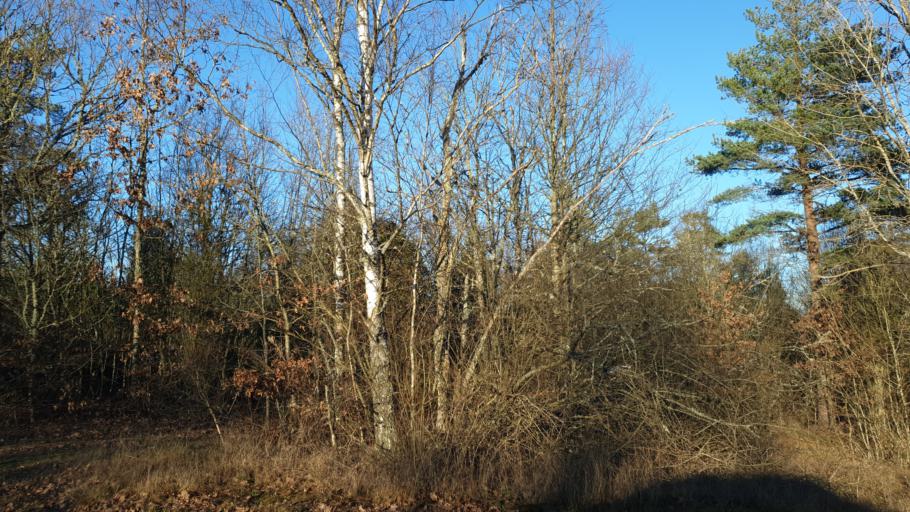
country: SE
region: Blekinge
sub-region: Ronneby Kommun
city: Brakne-Hoby
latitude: 56.2312
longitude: 15.1786
